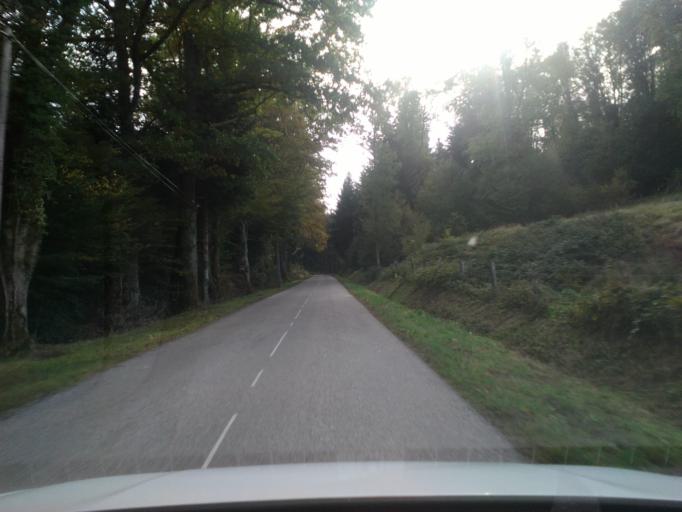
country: FR
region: Lorraine
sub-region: Departement des Vosges
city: Senones
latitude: 48.3502
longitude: 7.0012
